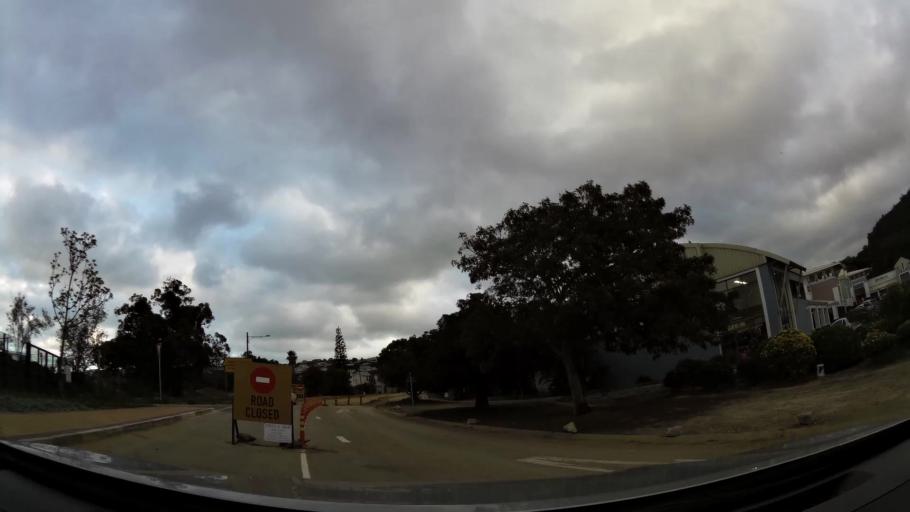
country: ZA
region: Western Cape
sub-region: Eden District Municipality
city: Plettenberg Bay
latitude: -34.0432
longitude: 23.3705
